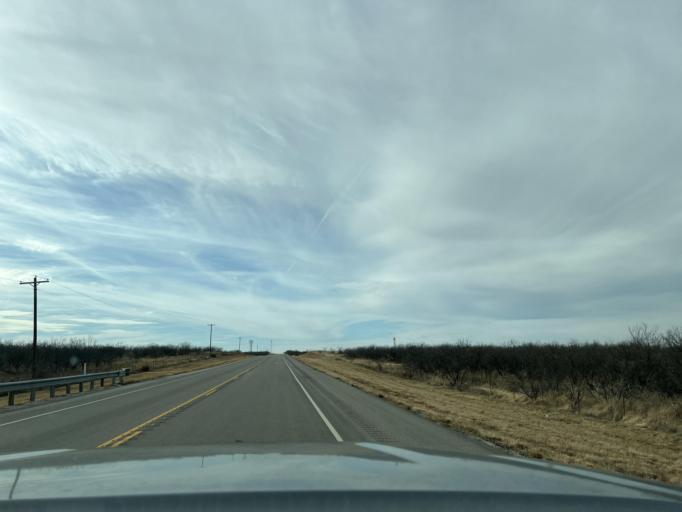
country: US
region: Texas
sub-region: Jones County
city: Anson
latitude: 32.7507
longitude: -99.7020
